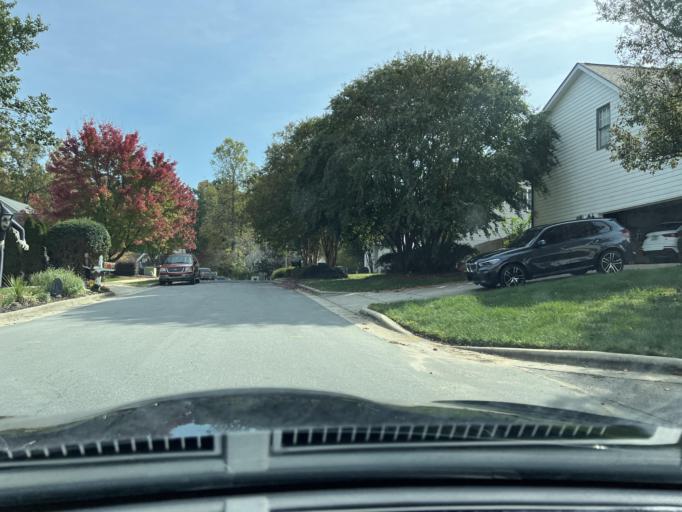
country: US
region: North Carolina
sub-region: Wake County
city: Wake Forest
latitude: 35.8971
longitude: -78.5812
